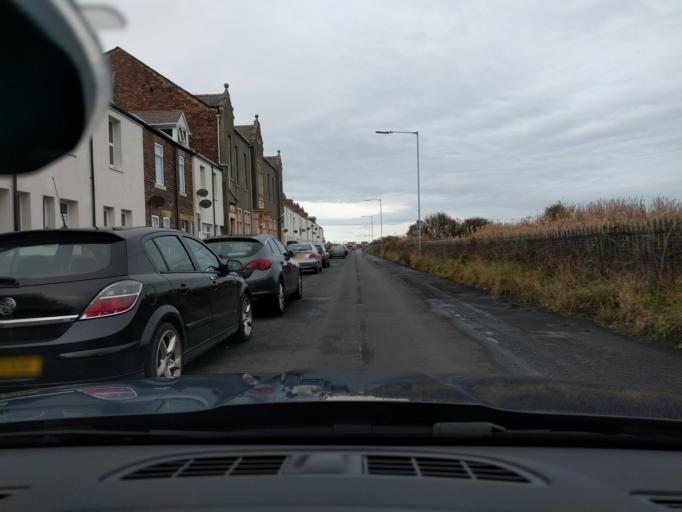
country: GB
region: England
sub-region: Northumberland
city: Blyth
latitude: 55.1454
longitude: -1.5208
